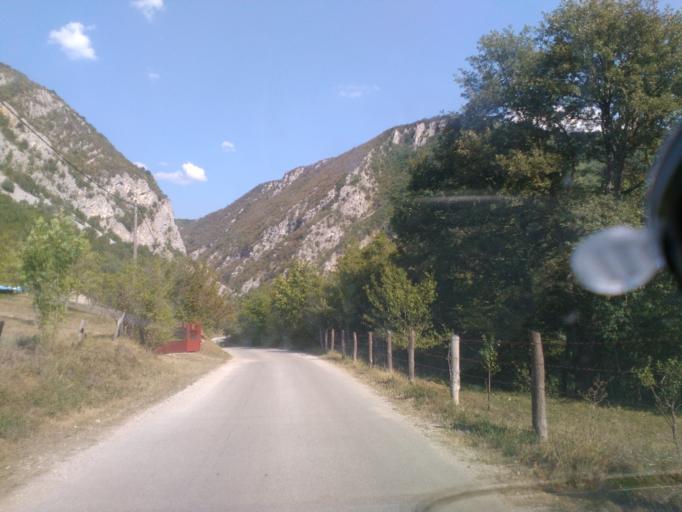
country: BA
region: Federation of Bosnia and Herzegovina
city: Orasac
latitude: 44.4941
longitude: 16.1395
